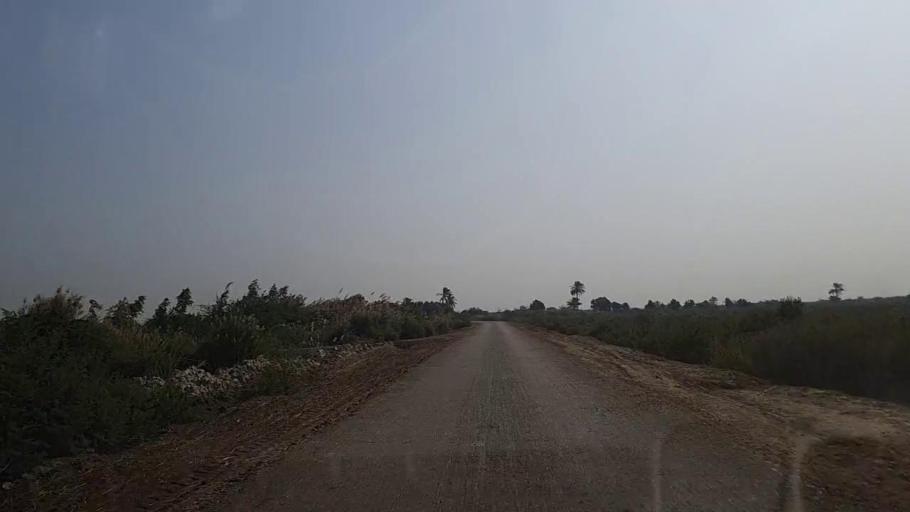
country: PK
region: Sindh
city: Keti Bandar
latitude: 24.2371
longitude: 67.6402
